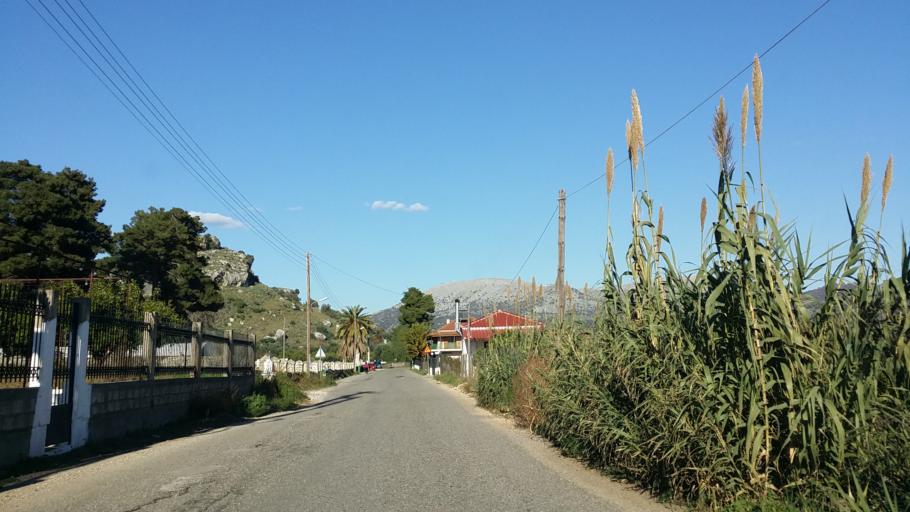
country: GR
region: West Greece
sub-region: Nomos Aitolias kai Akarnanias
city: Astakos
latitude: 38.5421
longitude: 21.0900
